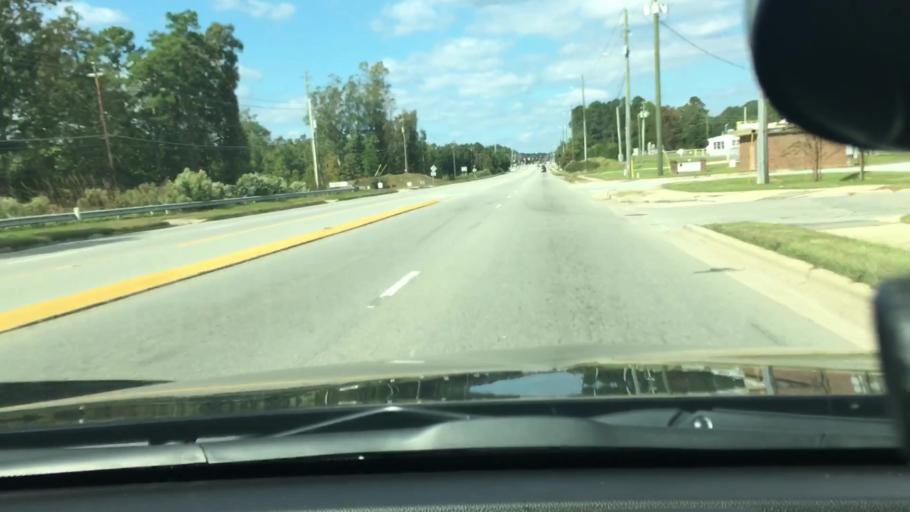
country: US
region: North Carolina
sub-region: Wake County
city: Apex
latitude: 35.7068
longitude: -78.8360
